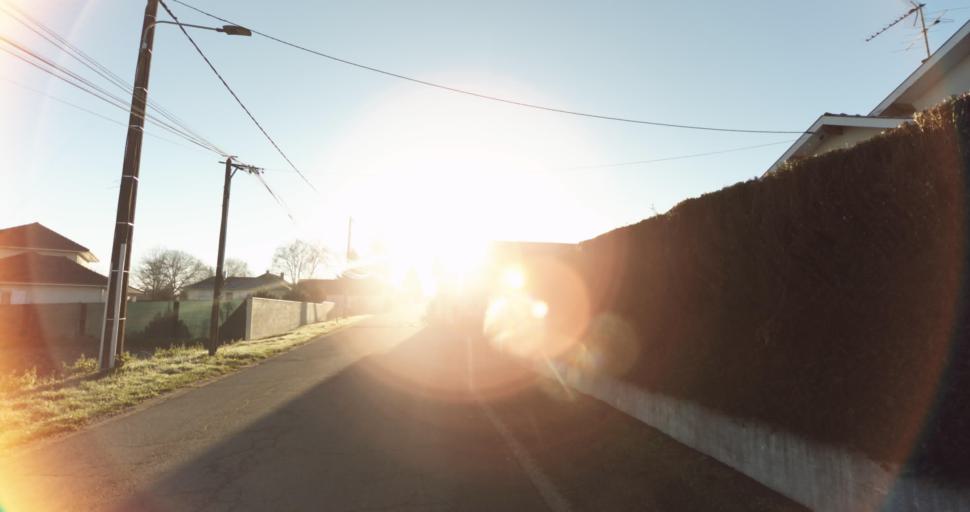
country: FR
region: Aquitaine
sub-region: Departement des Pyrenees-Atlantiques
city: Morlaas
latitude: 43.3352
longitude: -0.2731
